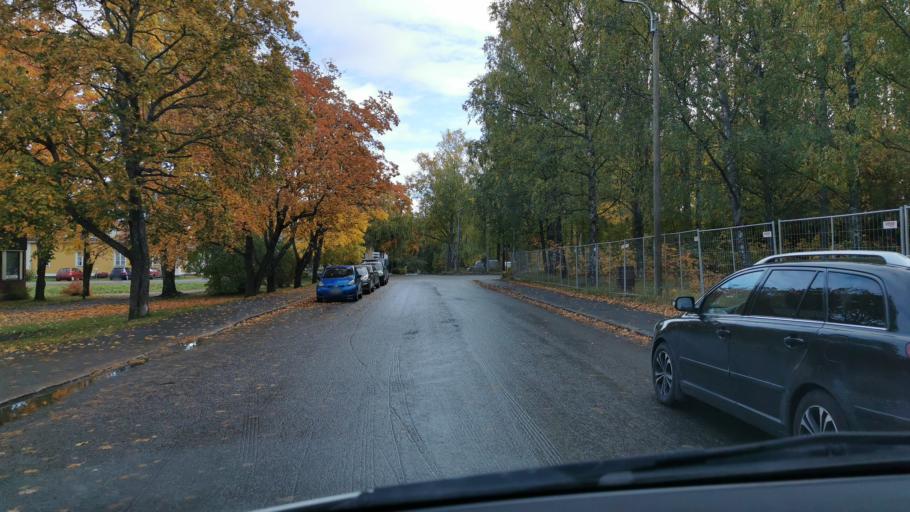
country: FI
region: Ostrobothnia
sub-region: Vaasa
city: Vaasa
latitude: 63.0925
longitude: 21.5619
